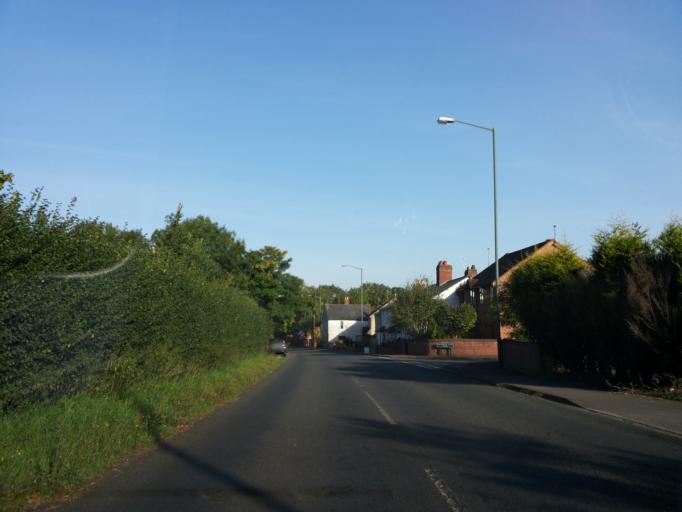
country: GB
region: England
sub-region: Warwickshire
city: Wroxall
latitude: 52.3538
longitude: -1.6962
